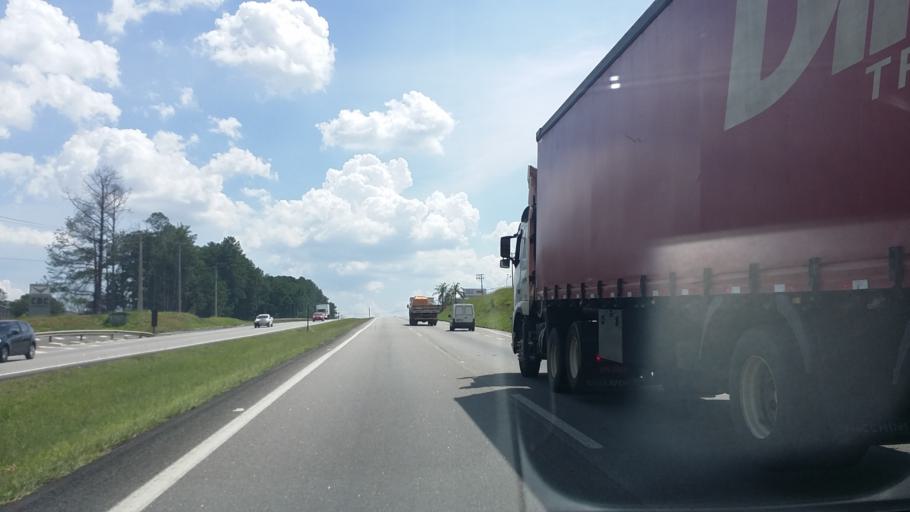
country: BR
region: Sao Paulo
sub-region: Itupeva
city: Itupeva
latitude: -23.1868
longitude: -46.9792
